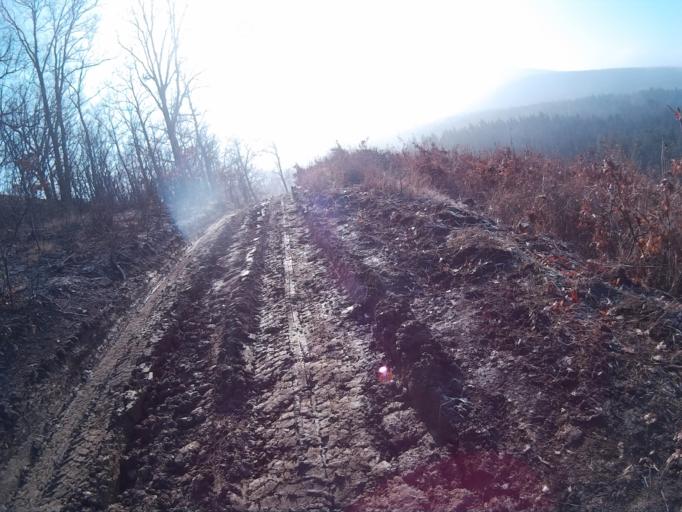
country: HU
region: Nograd
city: Batonyterenye
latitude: 47.9353
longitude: 19.8092
